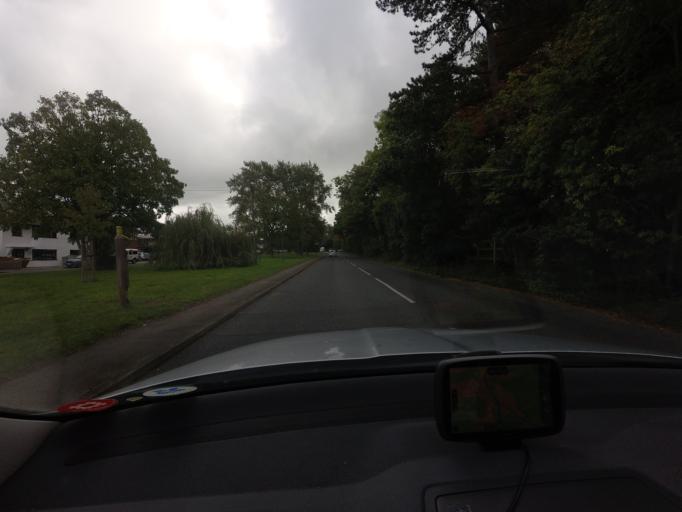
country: GB
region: England
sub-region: Kent
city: Tonbridge
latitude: 51.2186
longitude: 0.2356
